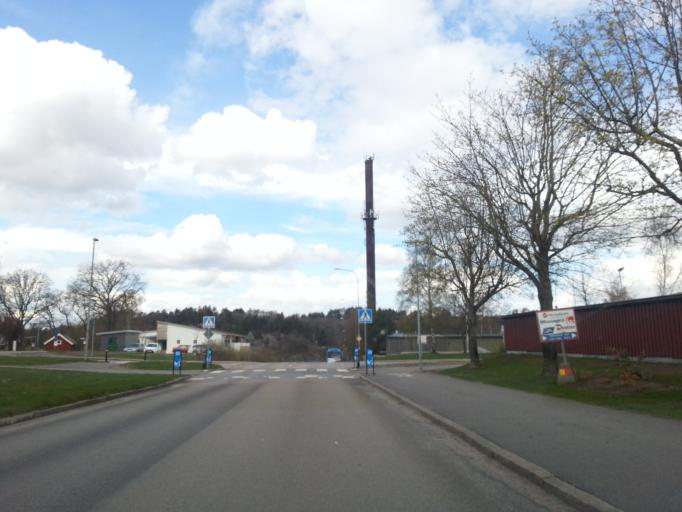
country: SE
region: Vaestra Goetaland
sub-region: Kungalvs Kommun
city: Kungalv
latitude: 57.8682
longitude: 11.9518
